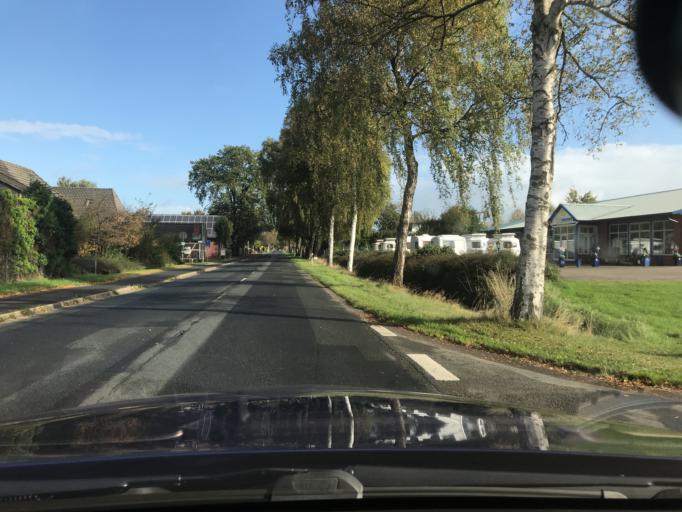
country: DE
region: Lower Saxony
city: Ahlerstedt
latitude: 53.4106
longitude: 9.4564
